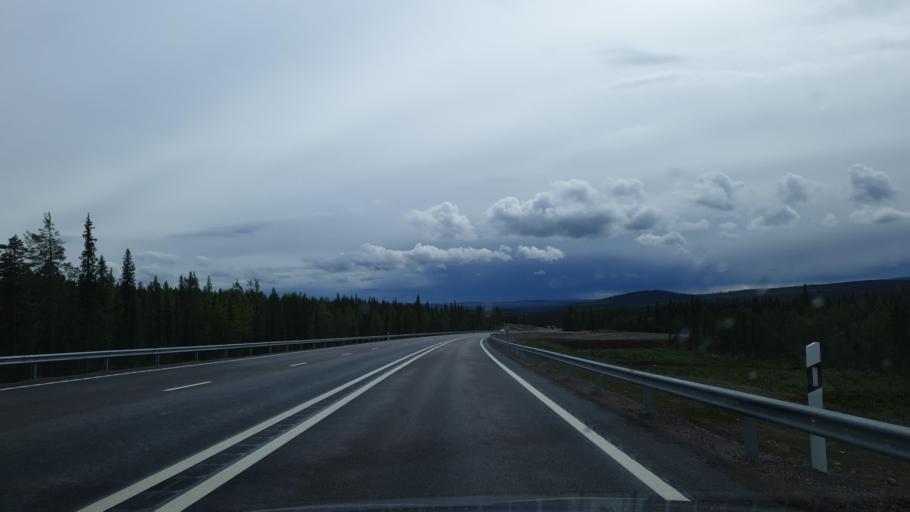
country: SE
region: Norrbotten
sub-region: Gallivare Kommun
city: Malmberget
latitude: 67.1851
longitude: 20.9749
